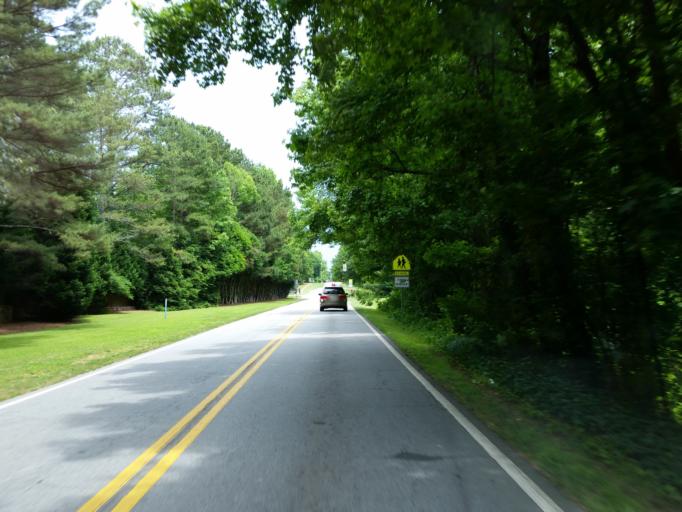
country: US
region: Georgia
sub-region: Fulton County
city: Roswell
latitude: 34.0653
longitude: -84.3884
